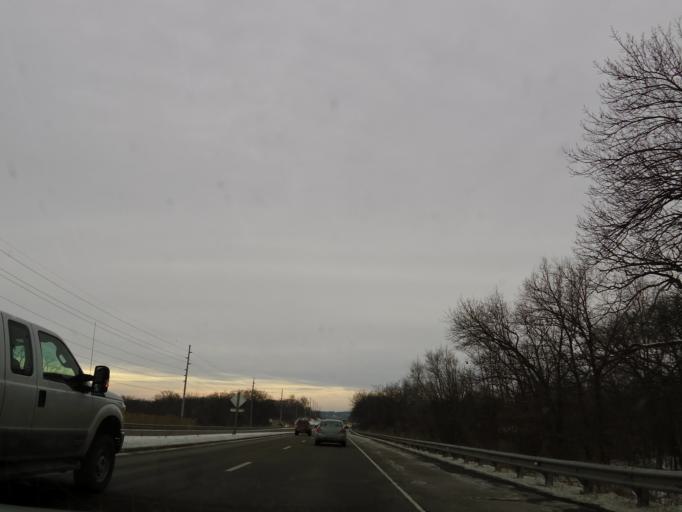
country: US
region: Illinois
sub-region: LaSalle County
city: Peru
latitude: 41.3362
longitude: -89.1201
